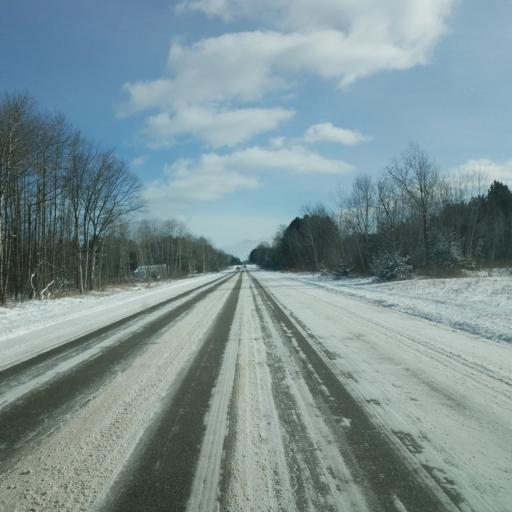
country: US
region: Michigan
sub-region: Osceola County
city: Evart
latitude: 43.9008
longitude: -85.1340
